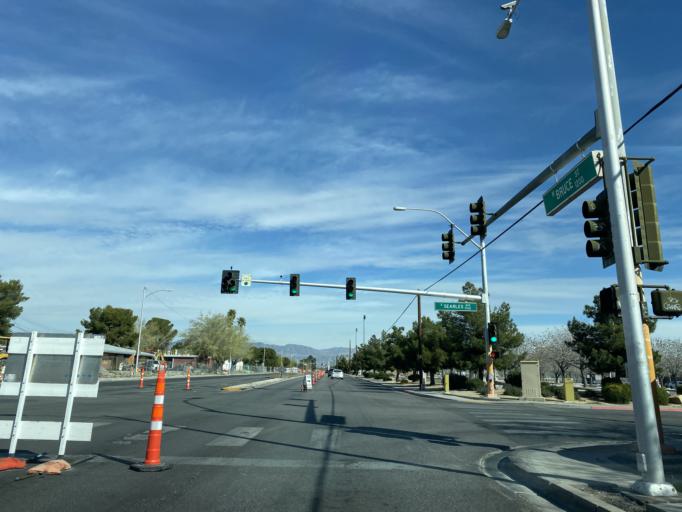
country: US
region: Nevada
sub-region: Clark County
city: Las Vegas
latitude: 36.1845
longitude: -115.1250
